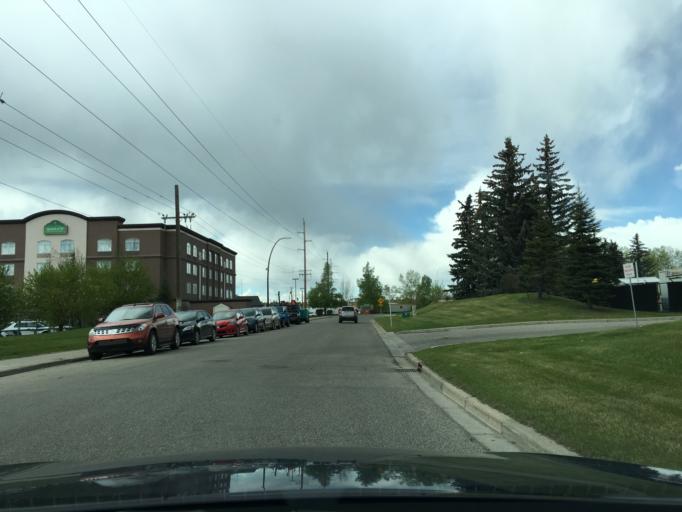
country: CA
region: Alberta
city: Calgary
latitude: 50.9069
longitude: -114.0596
